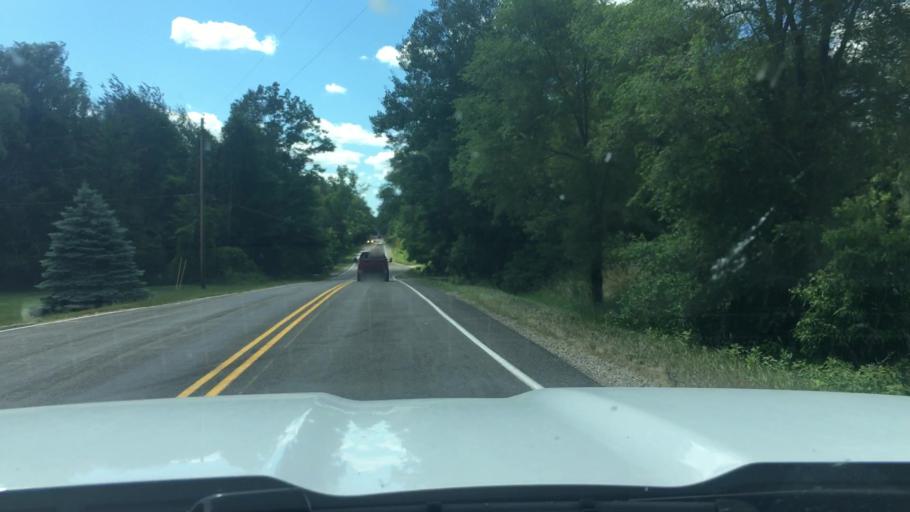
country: US
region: Michigan
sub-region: Kent County
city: Rockford
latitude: 43.1754
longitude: -85.6054
